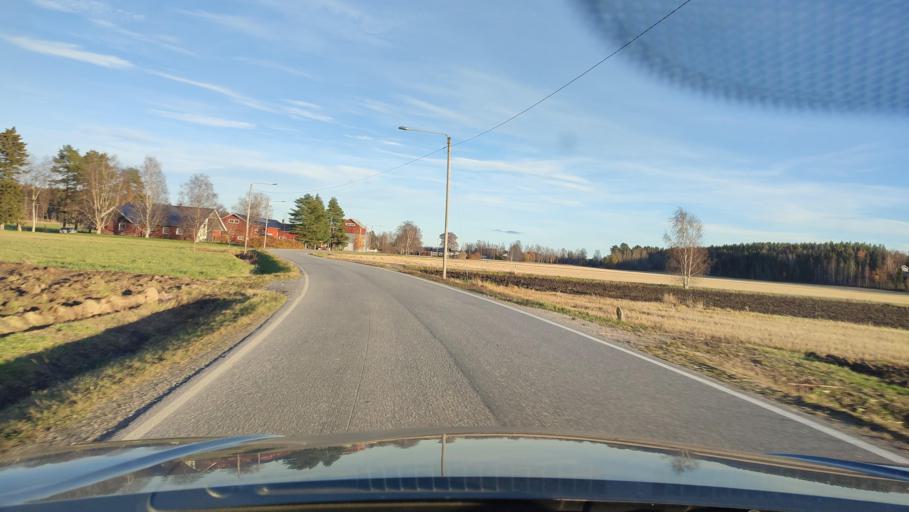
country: FI
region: Ostrobothnia
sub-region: Vaasa
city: Ristinummi
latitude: 62.9984
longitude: 21.7051
